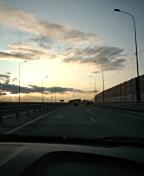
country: RU
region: Moskovskaya
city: Zhukovskiy
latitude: 55.5736
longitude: 38.1044
